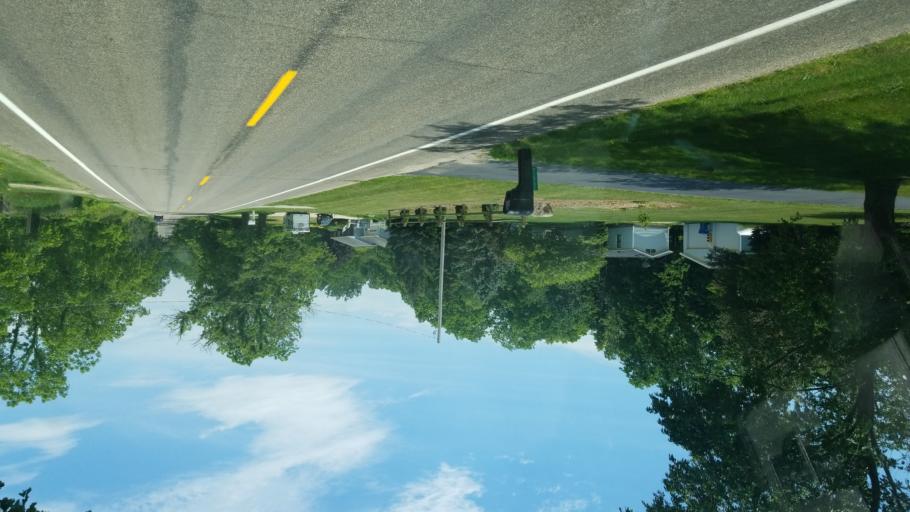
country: US
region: Michigan
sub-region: Eaton County
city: Charlotte
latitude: 42.6262
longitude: -84.8863
